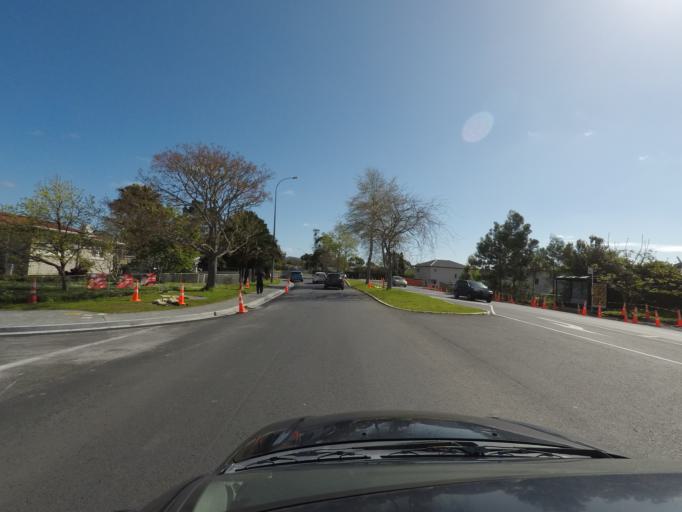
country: NZ
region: Auckland
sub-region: Auckland
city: Rosebank
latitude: -36.8583
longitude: 174.6162
